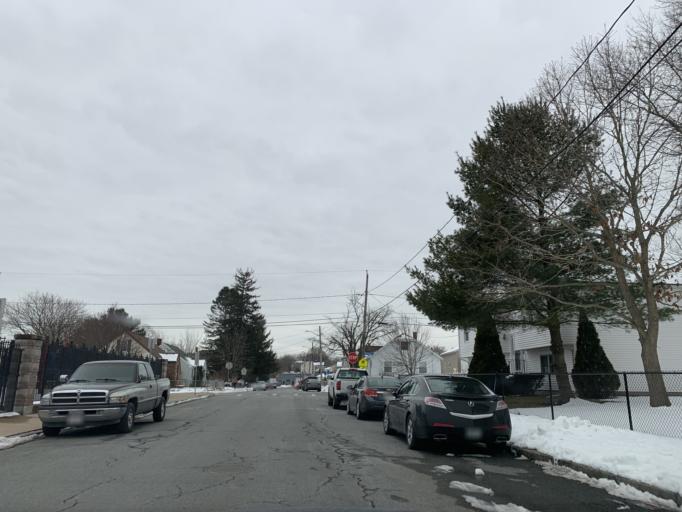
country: US
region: Massachusetts
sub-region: Bristol County
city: Fall River
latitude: 41.6863
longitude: -71.1534
